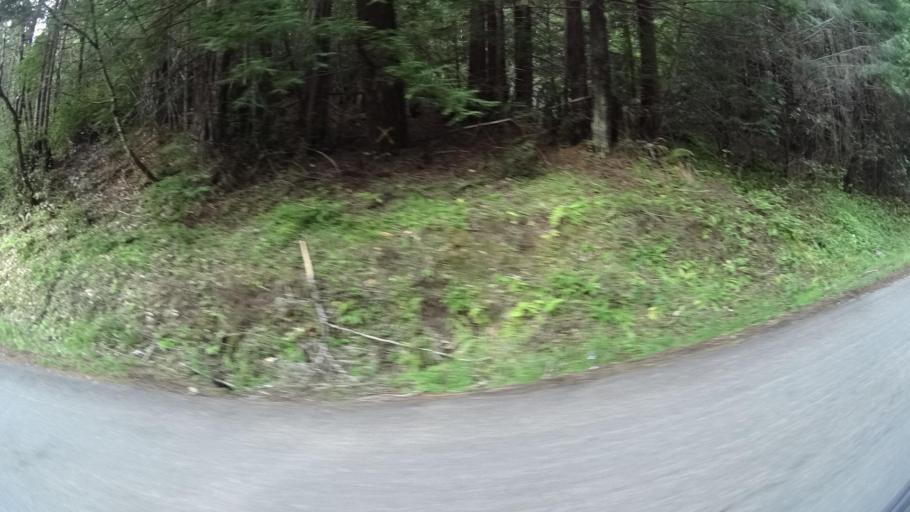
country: US
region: California
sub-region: Humboldt County
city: Redway
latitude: 40.2903
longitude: -123.8360
